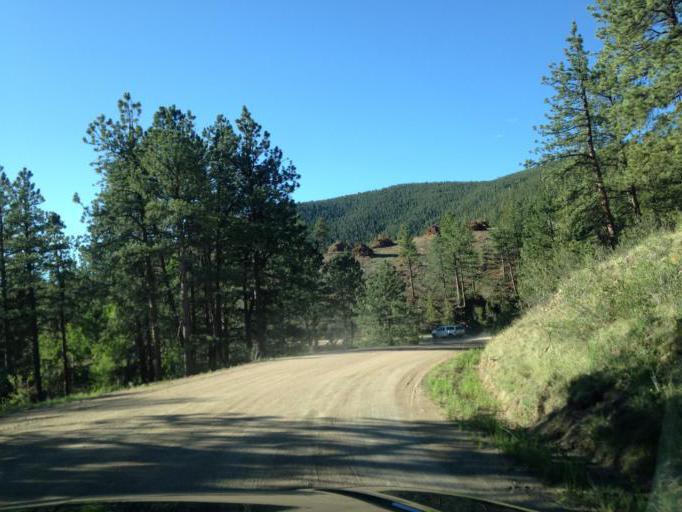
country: US
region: Colorado
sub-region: Jefferson County
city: Evergreen
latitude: 39.4041
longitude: -105.4967
